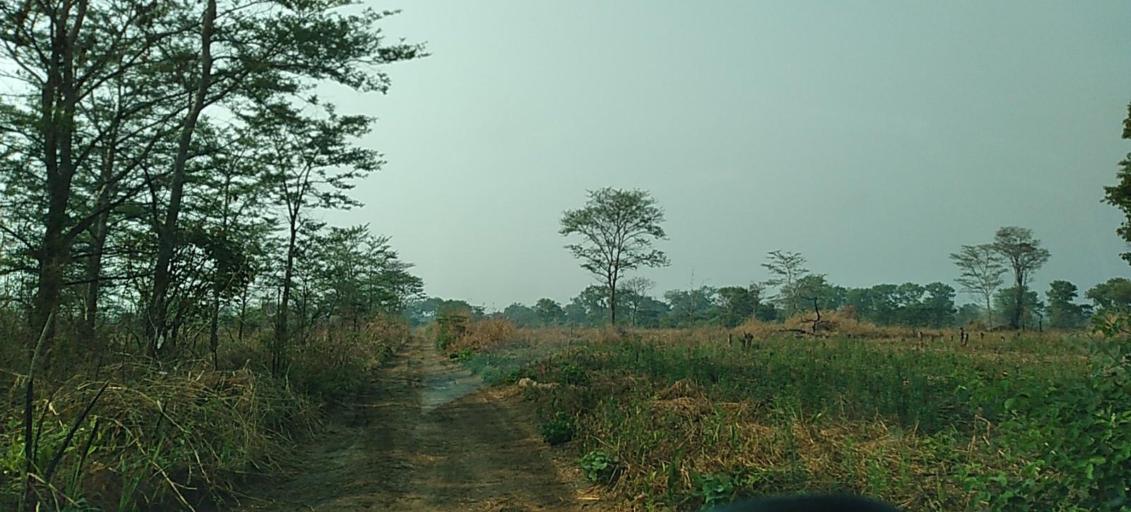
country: ZM
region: North-Western
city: Solwezi
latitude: -12.3782
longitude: 26.5637
